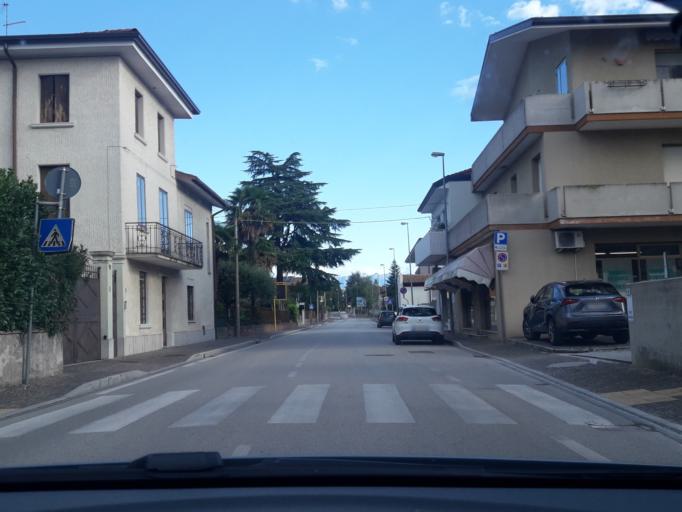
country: IT
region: Friuli Venezia Giulia
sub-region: Provincia di Udine
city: Passons
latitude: 46.0703
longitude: 13.1899
